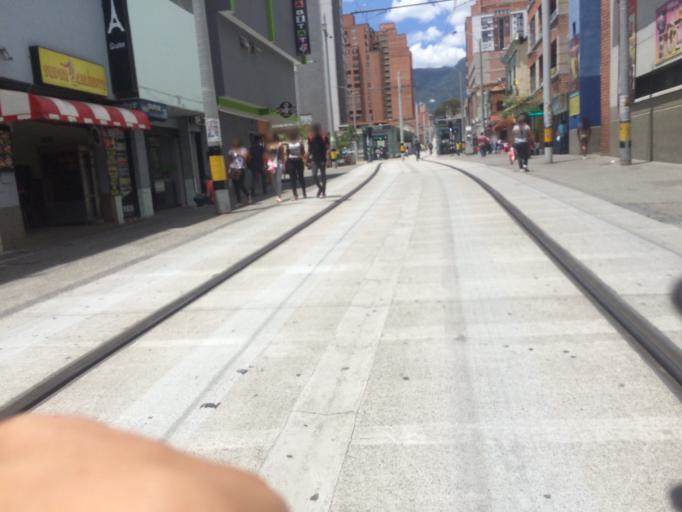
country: CO
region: Antioquia
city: Medellin
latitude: 6.2460
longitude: -75.5629
